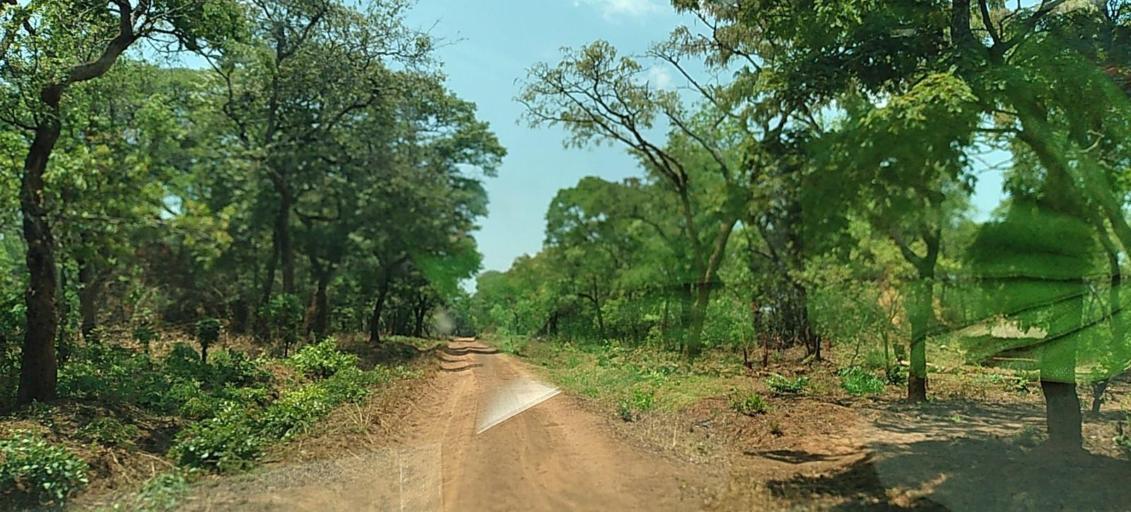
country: CD
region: Katanga
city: Kolwezi
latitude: -11.3579
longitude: 25.2077
